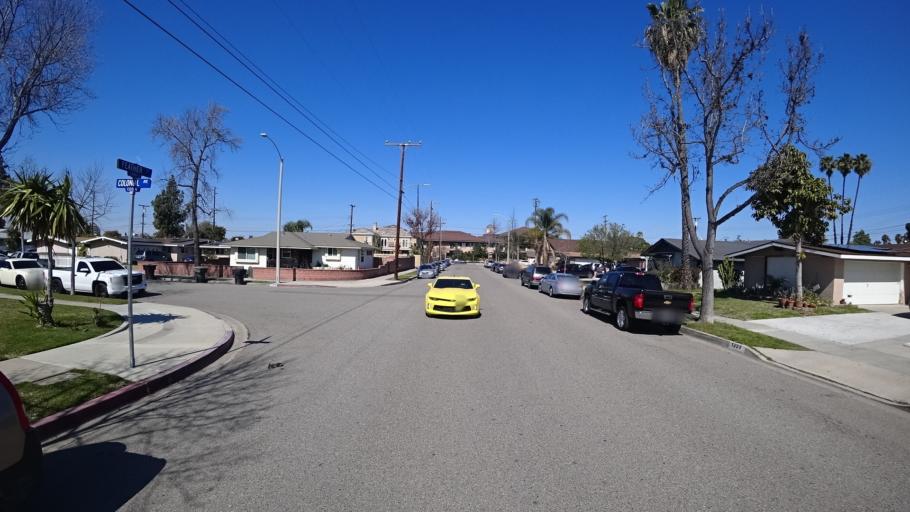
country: US
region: California
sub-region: Orange County
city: Anaheim
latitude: 33.8169
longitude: -117.9294
